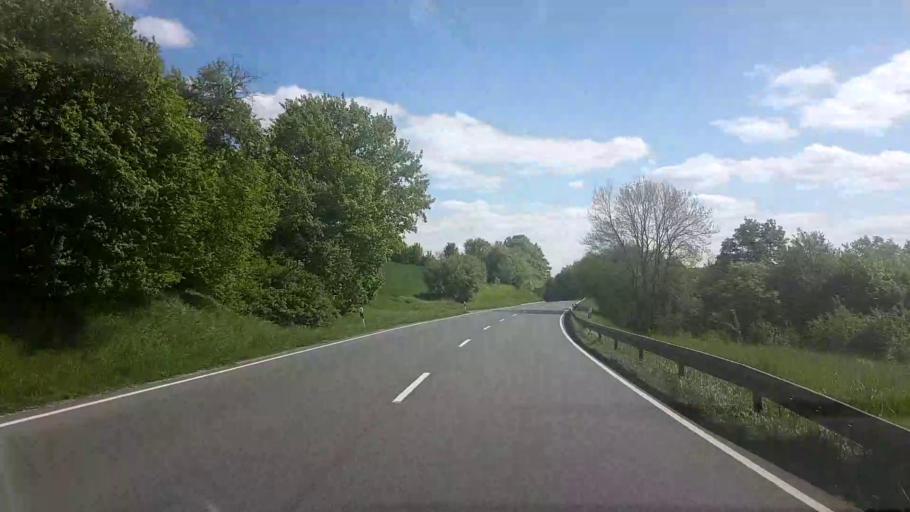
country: DE
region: Bavaria
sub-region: Regierungsbezirk Unterfranken
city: Untermerzbach
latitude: 50.0715
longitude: 10.8653
